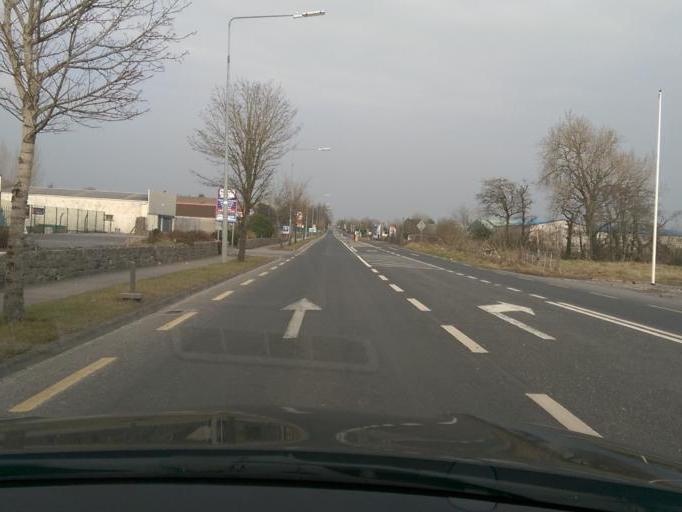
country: IE
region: Connaught
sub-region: Roscommon
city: Roscommon
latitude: 53.6347
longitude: -8.1799
